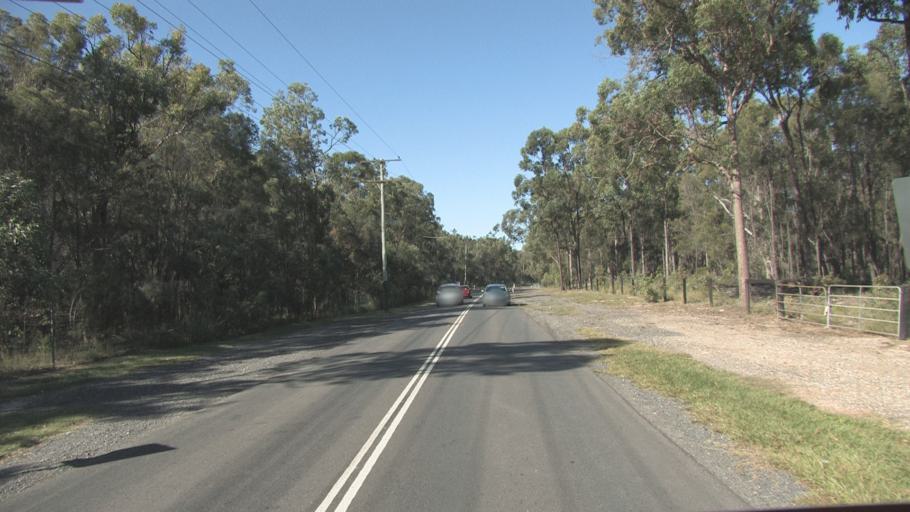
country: AU
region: Queensland
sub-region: Logan
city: Rochedale South
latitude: -27.5912
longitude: 153.1509
